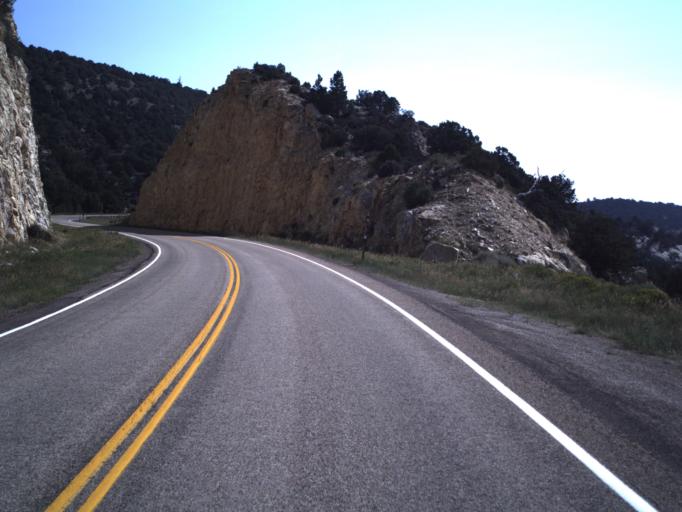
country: US
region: Utah
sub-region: Daggett County
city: Manila
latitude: 40.8959
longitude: -109.7145
